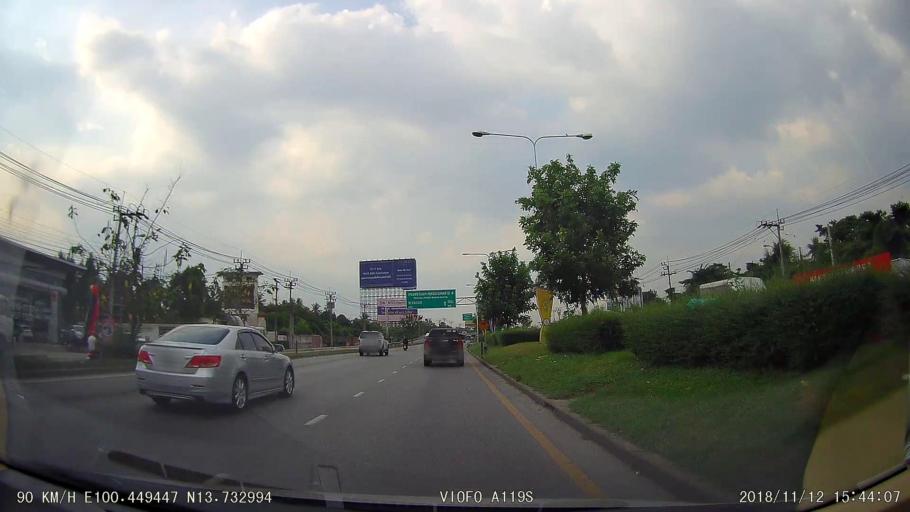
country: TH
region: Bangkok
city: Phasi Charoen
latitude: 13.7331
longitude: 100.4494
